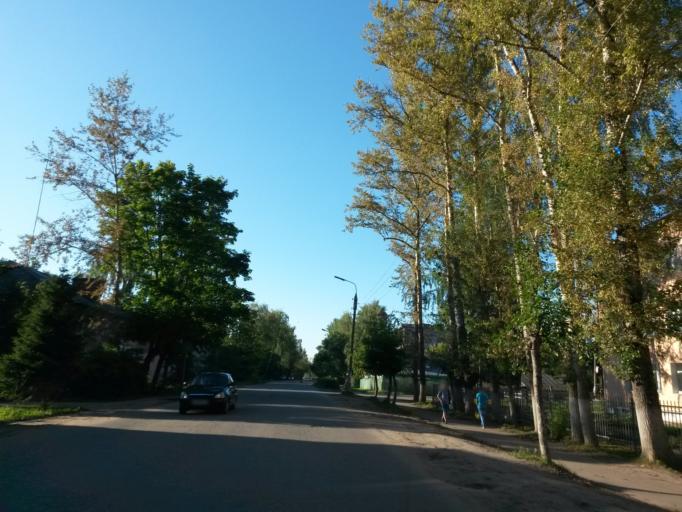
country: RU
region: Jaroslavl
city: Gavrilov-Yam
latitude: 57.3028
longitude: 39.8626
